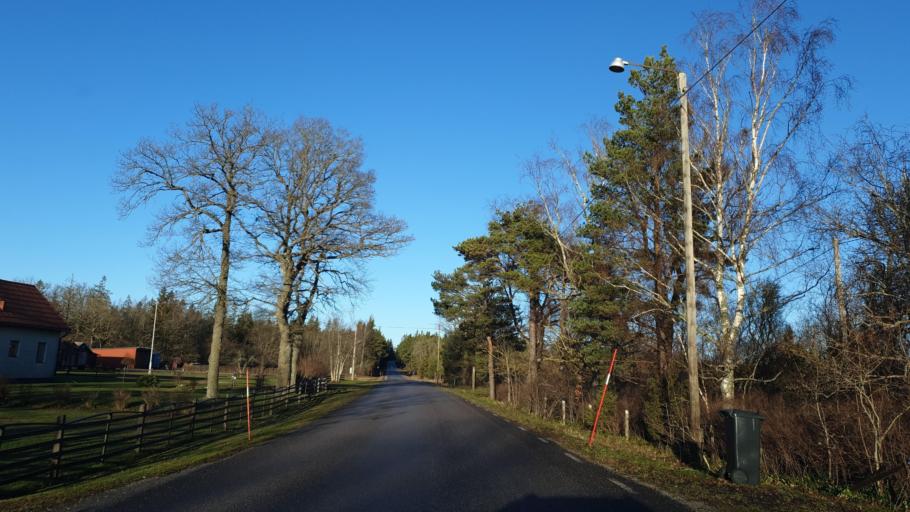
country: SE
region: Gotland
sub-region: Gotland
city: Slite
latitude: 57.7096
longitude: 18.7569
